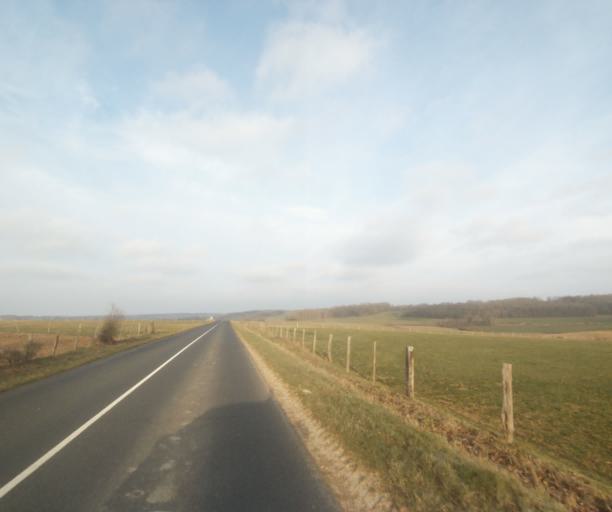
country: FR
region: Champagne-Ardenne
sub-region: Departement de la Marne
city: Sermaize-les-Bains
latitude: 48.7305
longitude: 4.9337
